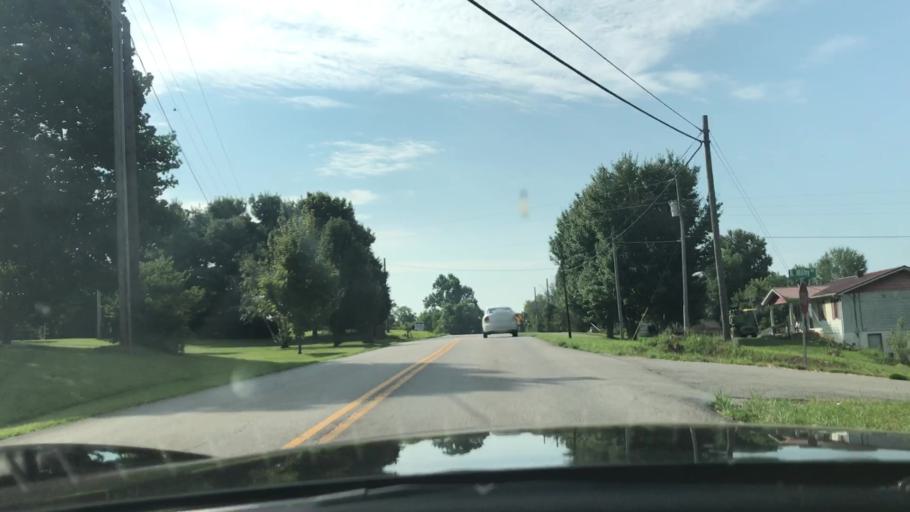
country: US
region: Kentucky
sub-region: Green County
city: Greensburg
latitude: 37.2649
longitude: -85.5613
